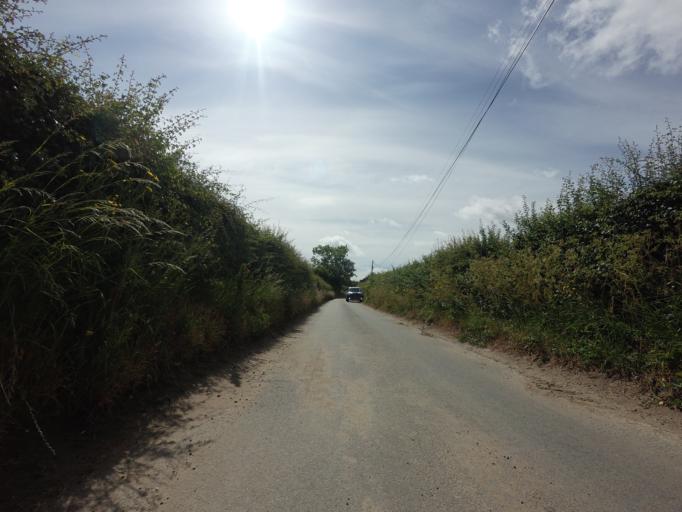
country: GB
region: England
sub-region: Greater London
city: Orpington
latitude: 51.3770
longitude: 0.1374
